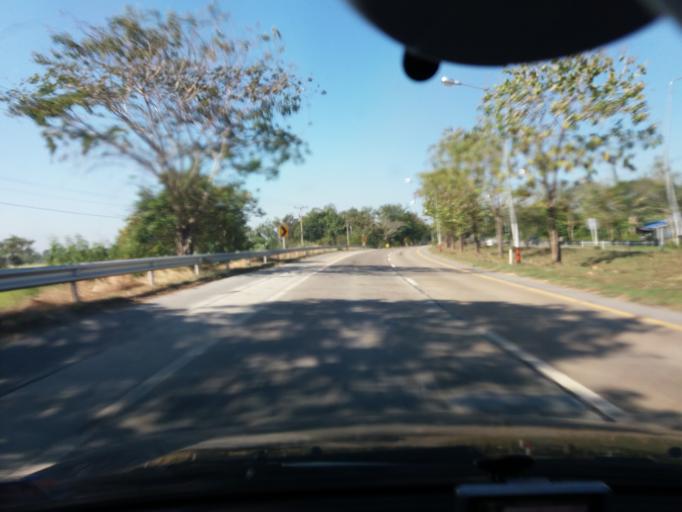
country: TH
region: Suphan Buri
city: Sam Chuk
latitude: 14.7886
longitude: 100.0995
